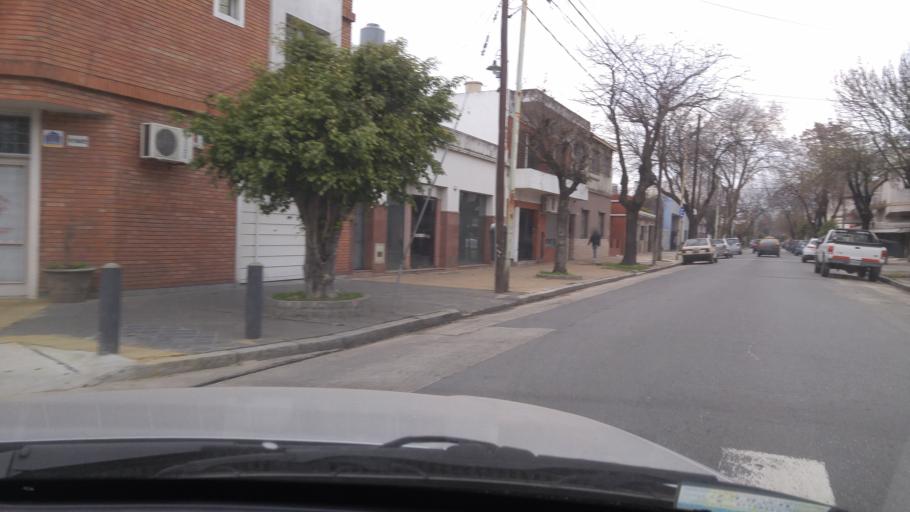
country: AR
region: Buenos Aires F.D.
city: Villa Santa Rita
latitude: -34.6140
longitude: -58.5195
